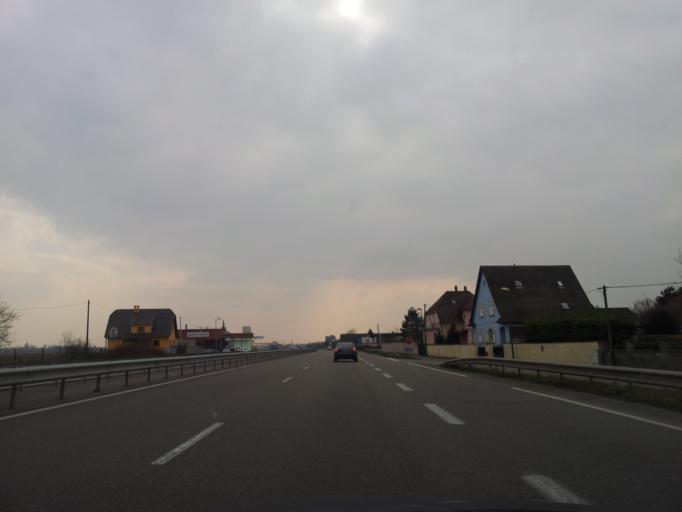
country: FR
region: Alsace
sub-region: Departement du Bas-Rhin
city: Erstein
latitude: 48.4218
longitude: 7.6397
